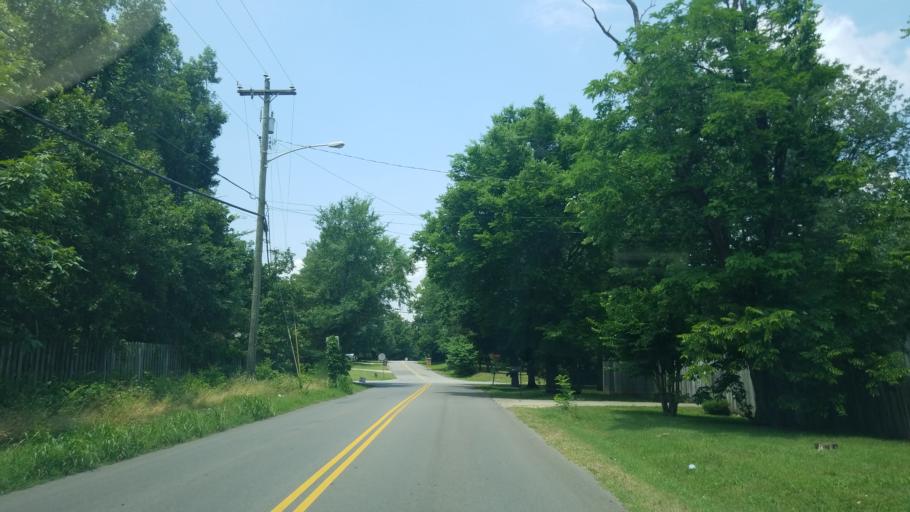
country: US
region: Tennessee
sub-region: Rutherford County
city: La Vergne
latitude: 36.0373
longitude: -86.5856
